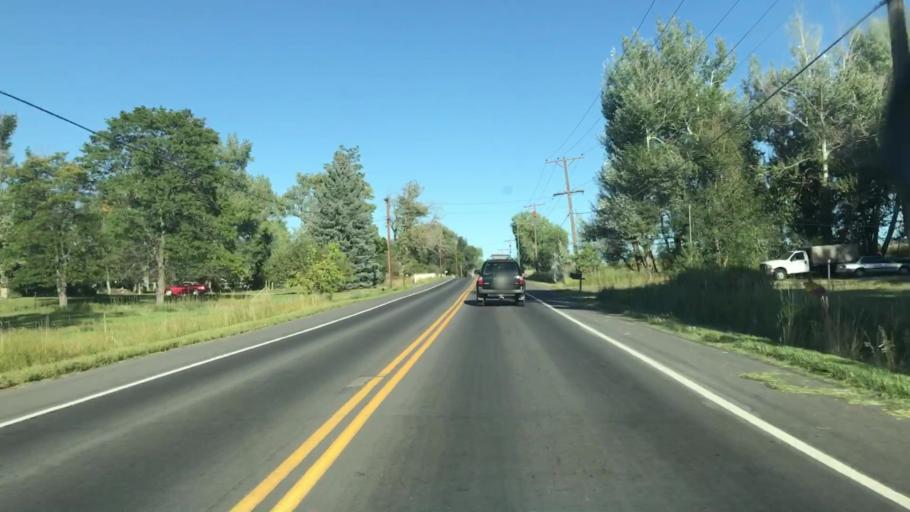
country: US
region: Colorado
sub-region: Boulder County
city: Louisville
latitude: 40.0001
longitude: -105.1662
